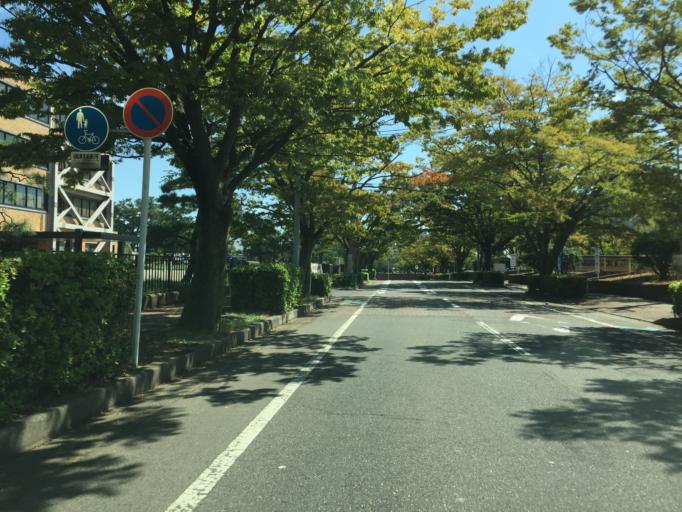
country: JP
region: Niigata
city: Niigata-shi
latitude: 37.9277
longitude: 139.0422
